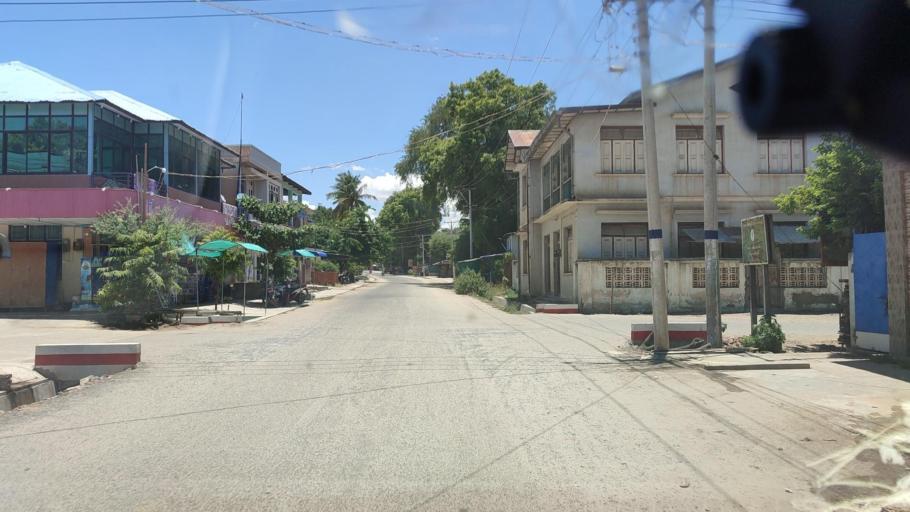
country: MM
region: Magway
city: Chauk
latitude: 20.8333
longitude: 94.7408
